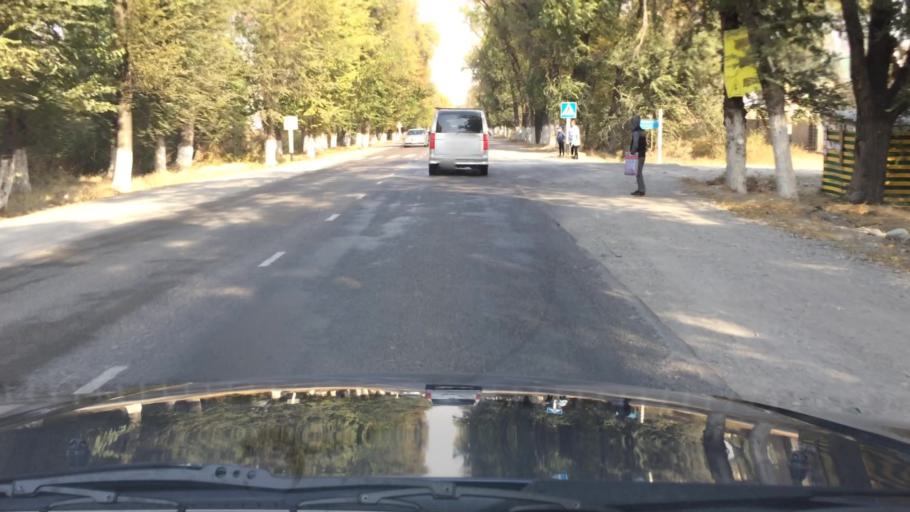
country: KG
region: Chuy
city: Lebedinovka
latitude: 42.9207
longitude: 74.6895
